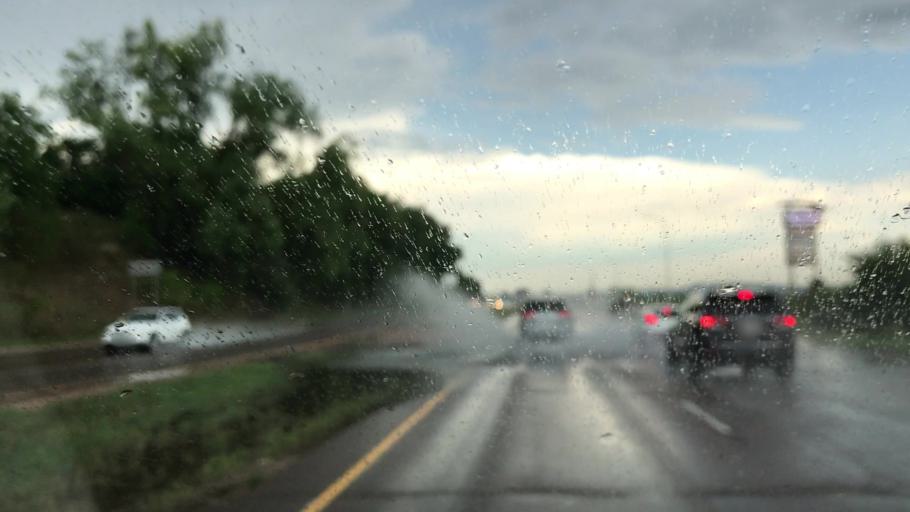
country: US
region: Colorado
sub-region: El Paso County
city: Colorado Springs
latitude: 38.8009
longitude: -104.8221
